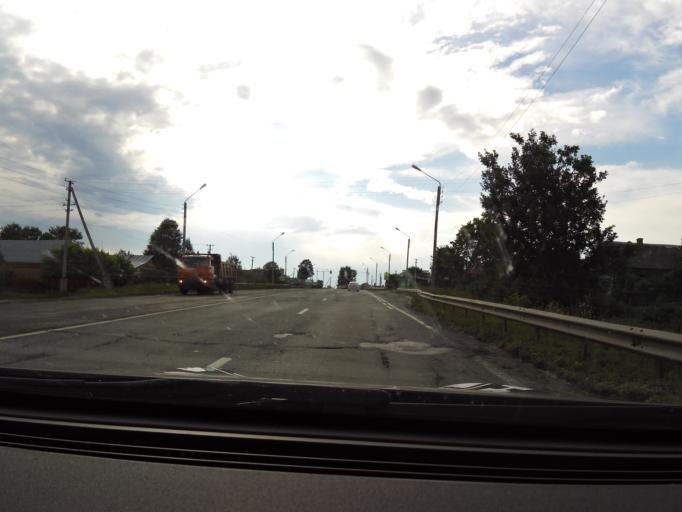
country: RU
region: Vladimir
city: Novovyazniki
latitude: 56.1720
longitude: 42.4245
